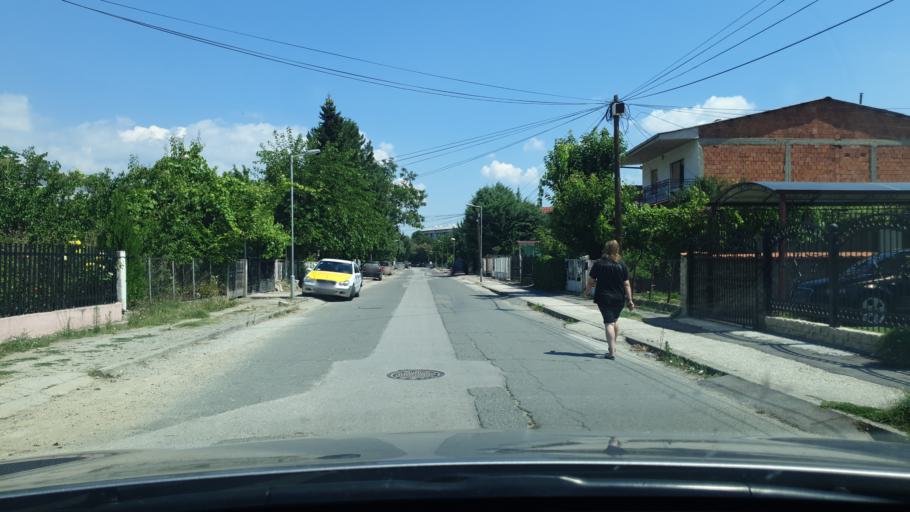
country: MK
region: Kisela Voda
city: Kisela Voda
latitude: 41.9406
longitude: 21.5164
